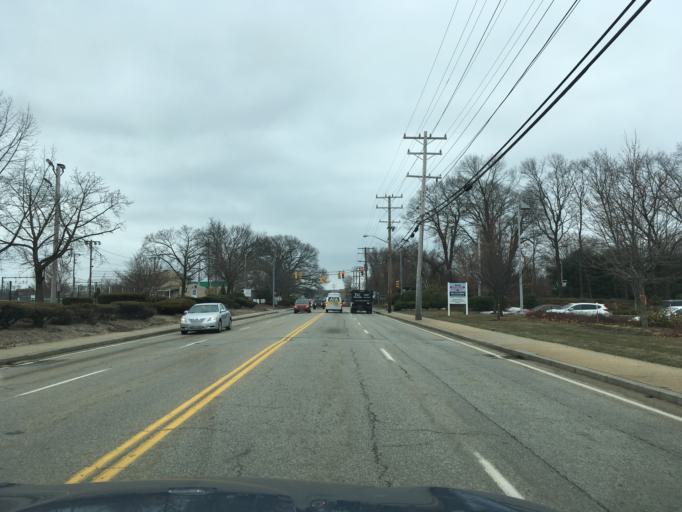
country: US
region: Rhode Island
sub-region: Kent County
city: Warwick
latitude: 41.7205
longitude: -71.4461
